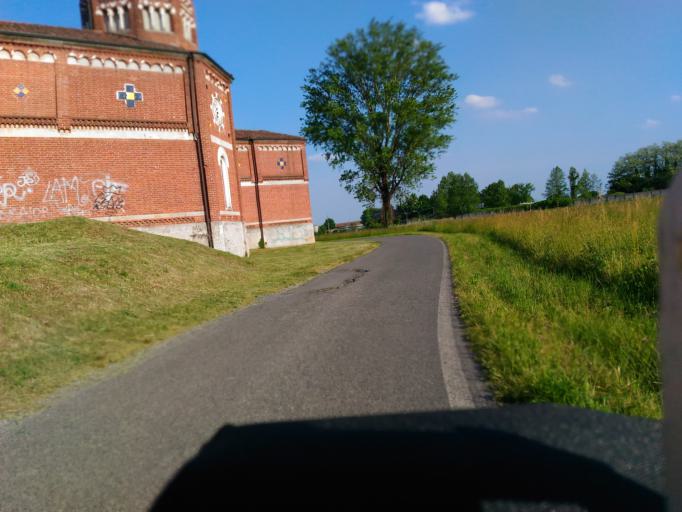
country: IT
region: Lombardy
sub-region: Provincia di Lodi
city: Montanaso Lombardo
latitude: 45.3210
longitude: 9.4722
